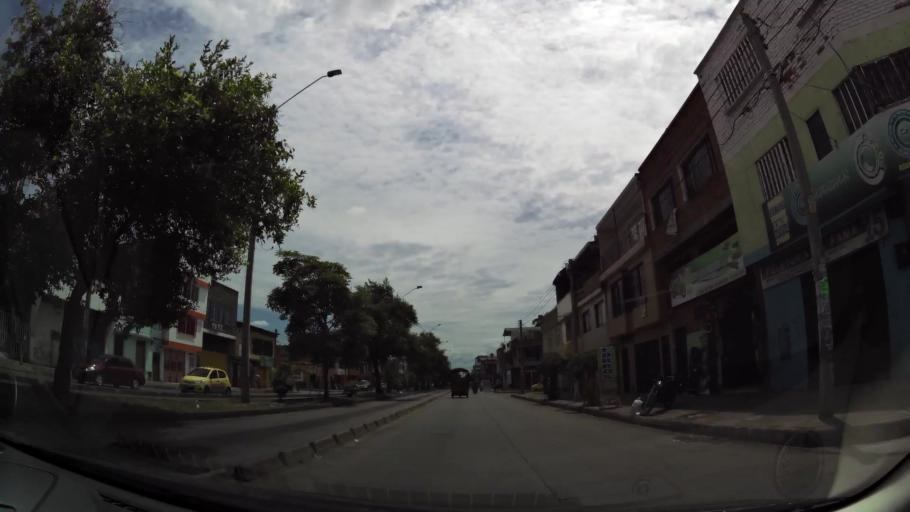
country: CO
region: Valle del Cauca
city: Cali
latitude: 3.4452
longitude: -76.5135
